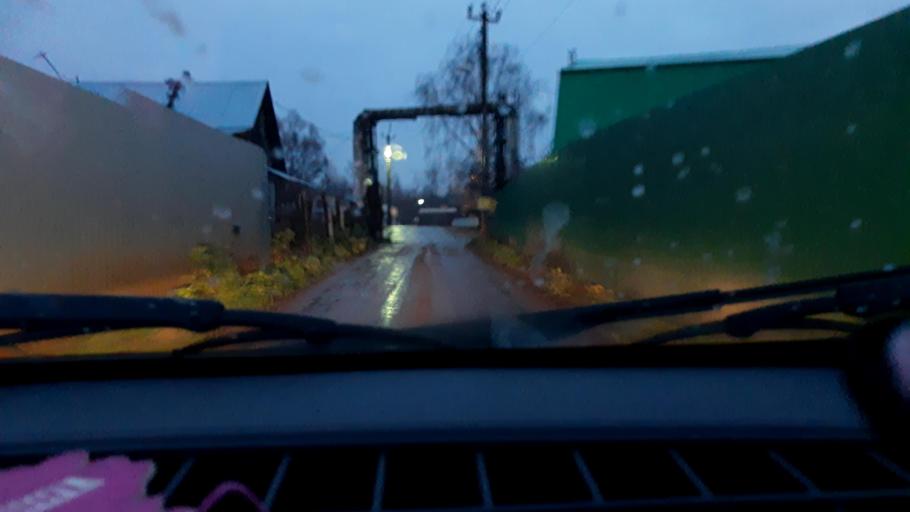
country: RU
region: Bashkortostan
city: Ufa
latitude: 54.8098
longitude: 56.1549
